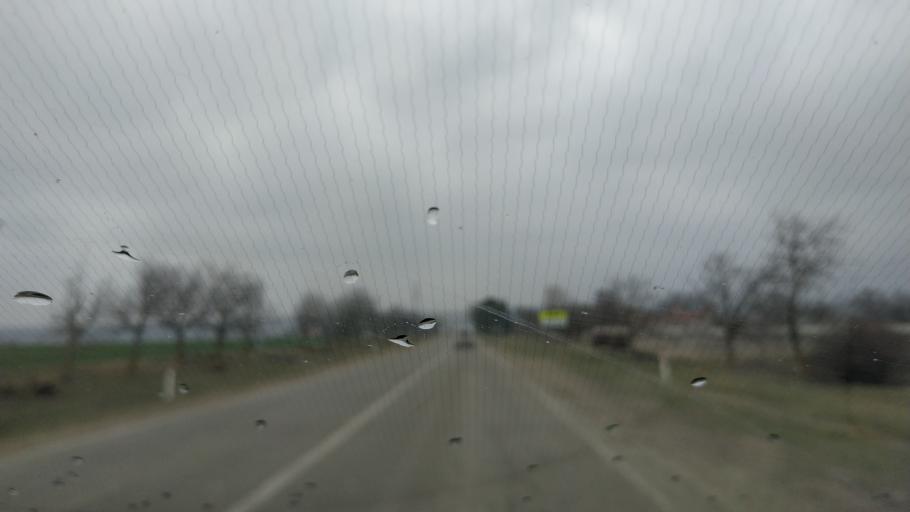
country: MD
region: Gagauzia
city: Comrat
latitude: 46.2477
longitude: 28.7607
